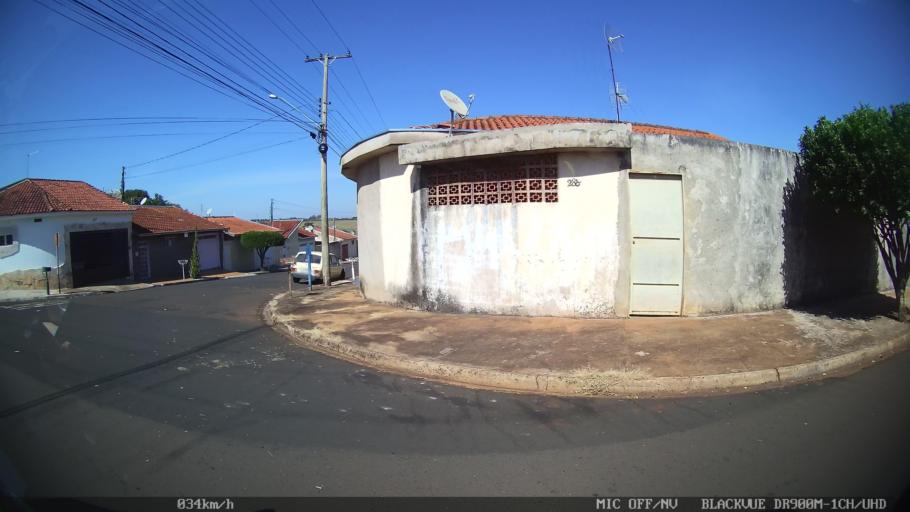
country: BR
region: Sao Paulo
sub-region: Batatais
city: Batatais
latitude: -20.8890
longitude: -47.5720
